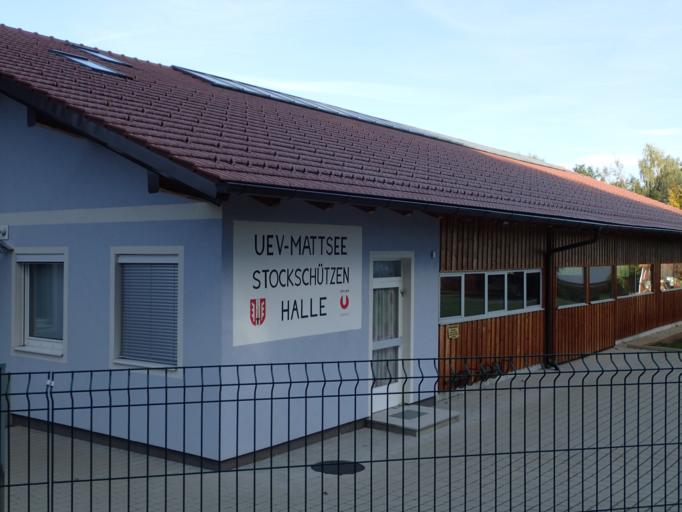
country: AT
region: Salzburg
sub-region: Politischer Bezirk Salzburg-Umgebung
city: Mattsee
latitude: 47.9715
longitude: 13.0990
